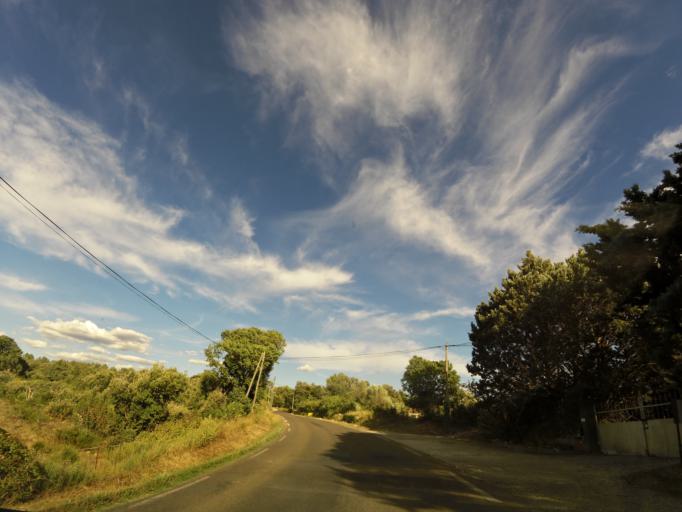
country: FR
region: Languedoc-Roussillon
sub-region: Departement de l'Herault
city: Boisseron
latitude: 43.7780
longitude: 4.0620
